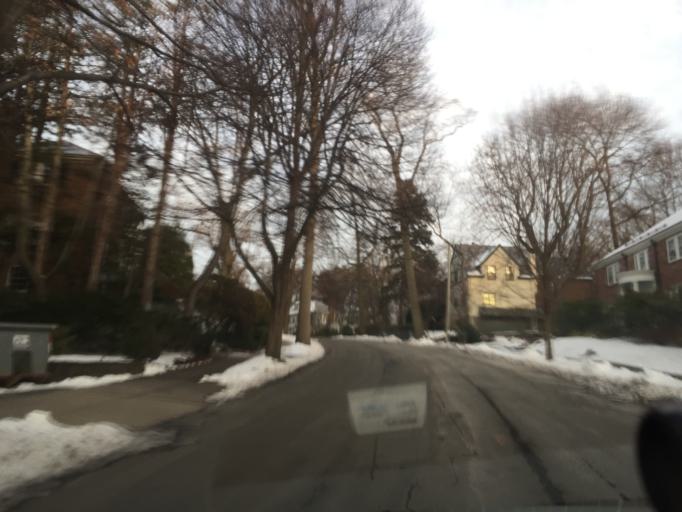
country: US
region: Massachusetts
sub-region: Norfolk County
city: Brookline
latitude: 42.3309
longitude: -71.1517
